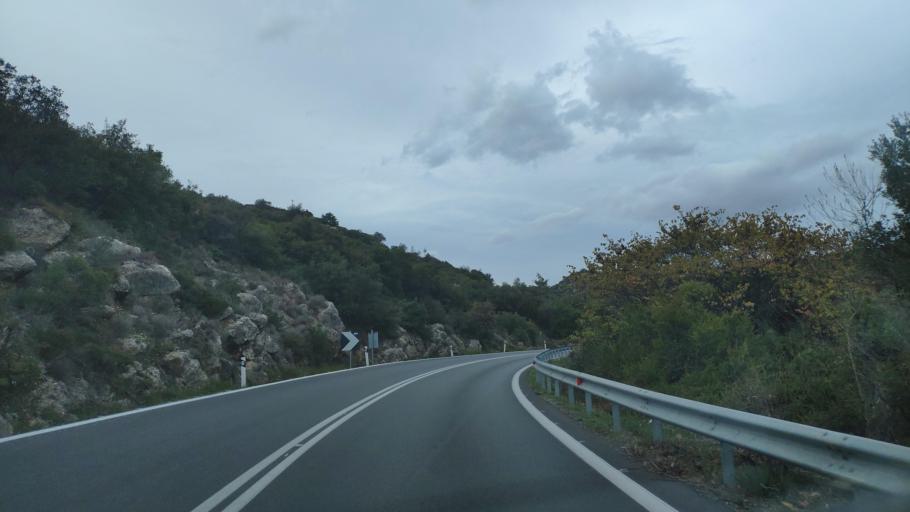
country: GR
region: Peloponnese
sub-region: Nomos Korinthias
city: Ayios Vasilios
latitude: 37.7663
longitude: 22.7281
